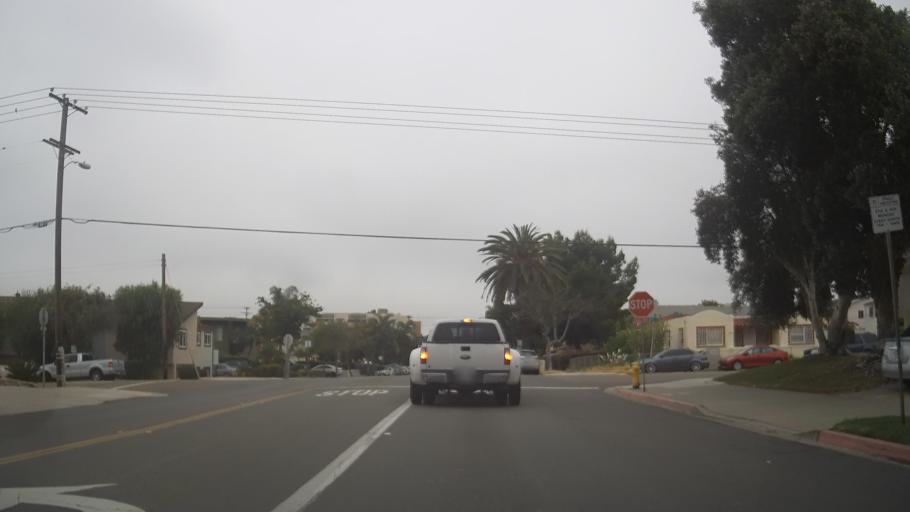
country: US
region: California
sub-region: San Diego County
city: San Diego
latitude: 32.7518
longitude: -117.1388
